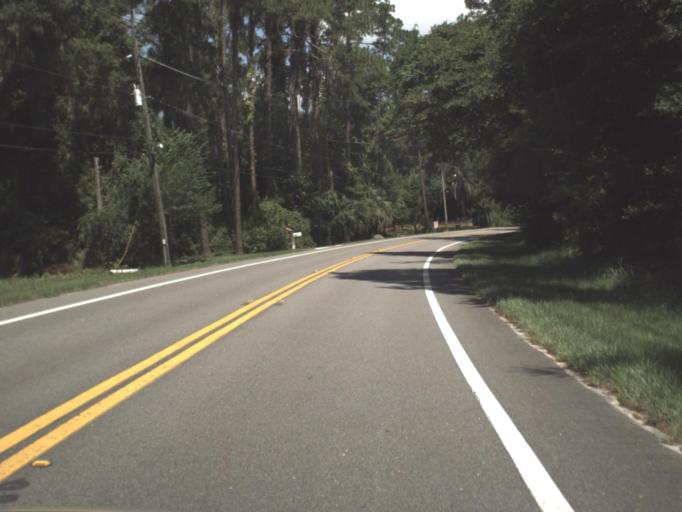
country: US
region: Florida
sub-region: Clay County
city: Green Cove Springs
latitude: 30.0372
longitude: -81.6655
